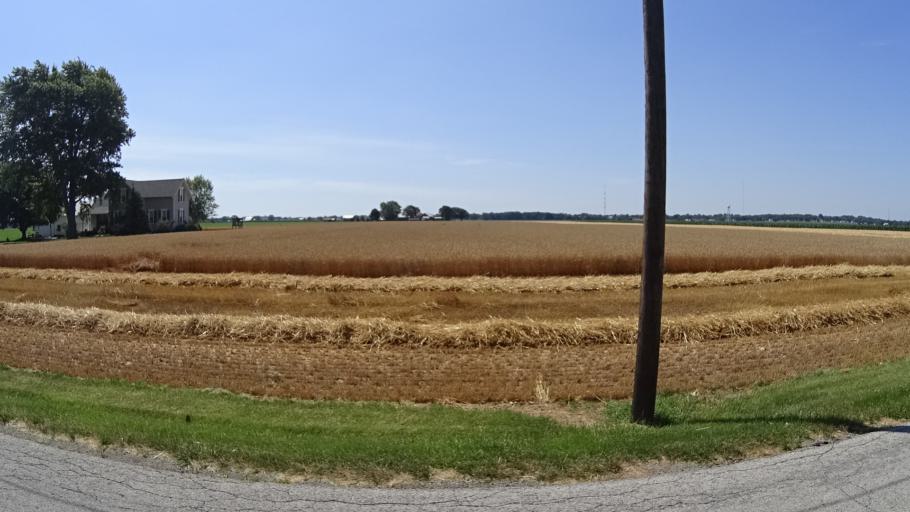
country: US
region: Ohio
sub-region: Erie County
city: Sandusky
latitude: 41.4245
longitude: -82.7872
